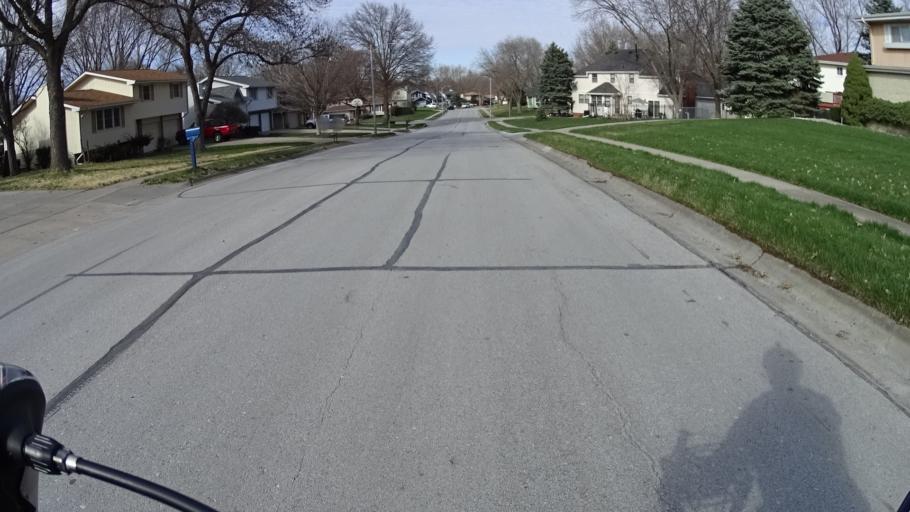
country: US
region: Nebraska
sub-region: Sarpy County
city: Offutt Air Force Base
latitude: 41.1161
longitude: -95.9595
